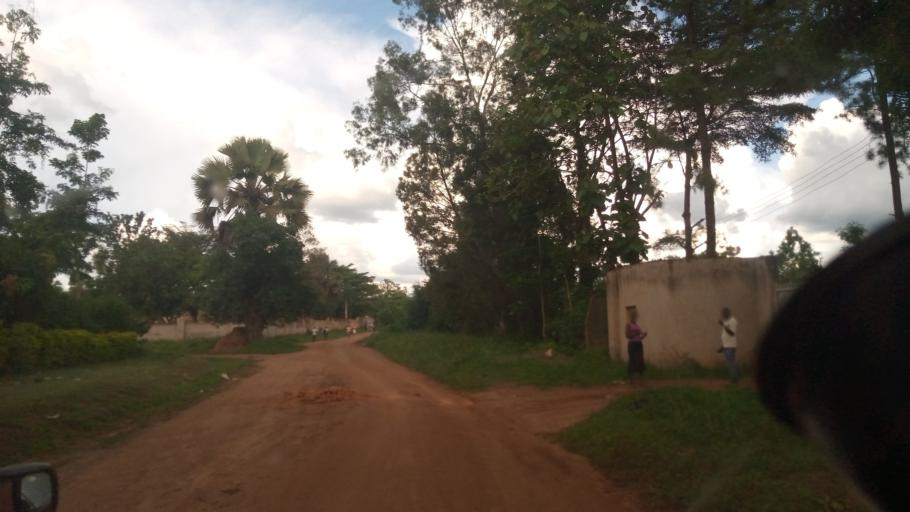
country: UG
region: Northern Region
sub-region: Lira District
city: Lira
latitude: 2.2383
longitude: 32.9020
